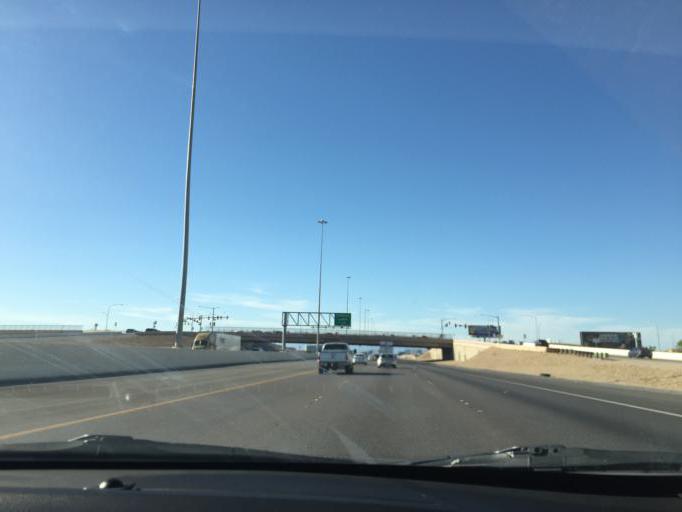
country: US
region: Nevada
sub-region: Clark County
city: Enterprise
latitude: 36.0107
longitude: -115.1802
